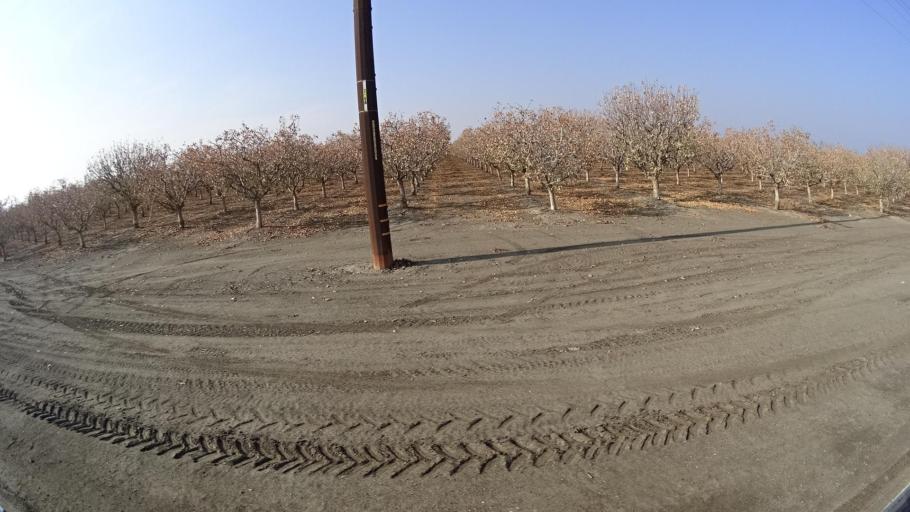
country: US
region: California
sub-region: Kern County
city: Buttonwillow
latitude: 35.3594
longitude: -119.4477
